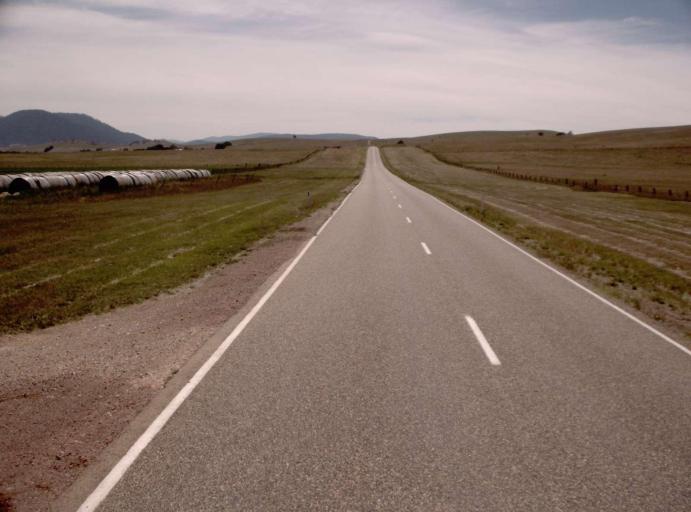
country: AU
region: Victoria
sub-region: Alpine
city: Mount Beauty
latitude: -36.9950
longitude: 147.6830
